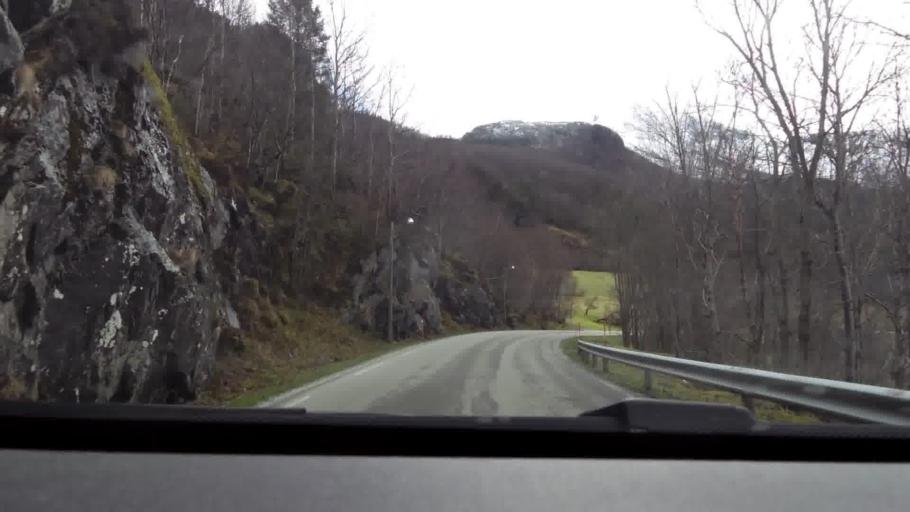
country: NO
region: More og Romsdal
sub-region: Gjemnes
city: Batnfjordsora
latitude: 62.9283
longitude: 7.5968
